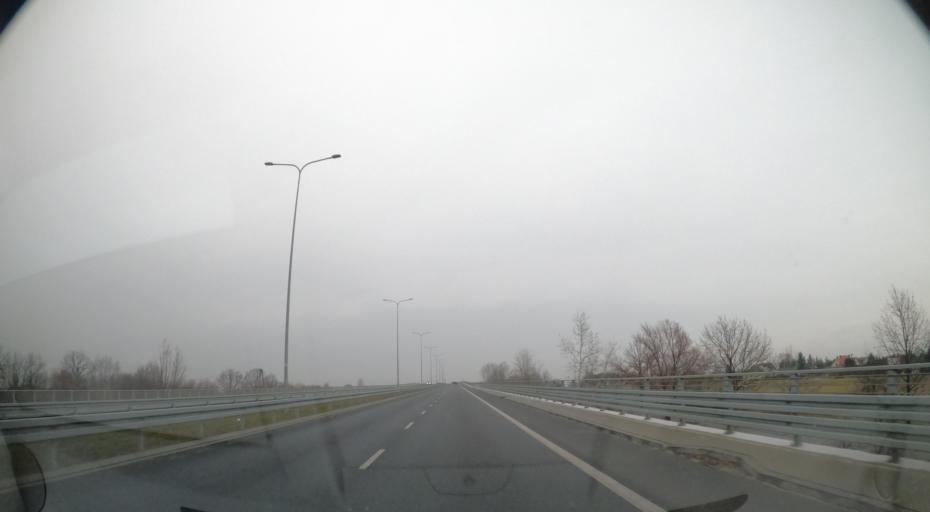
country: PL
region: Masovian Voivodeship
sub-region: Radom
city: Radom
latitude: 51.4052
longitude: 21.2018
